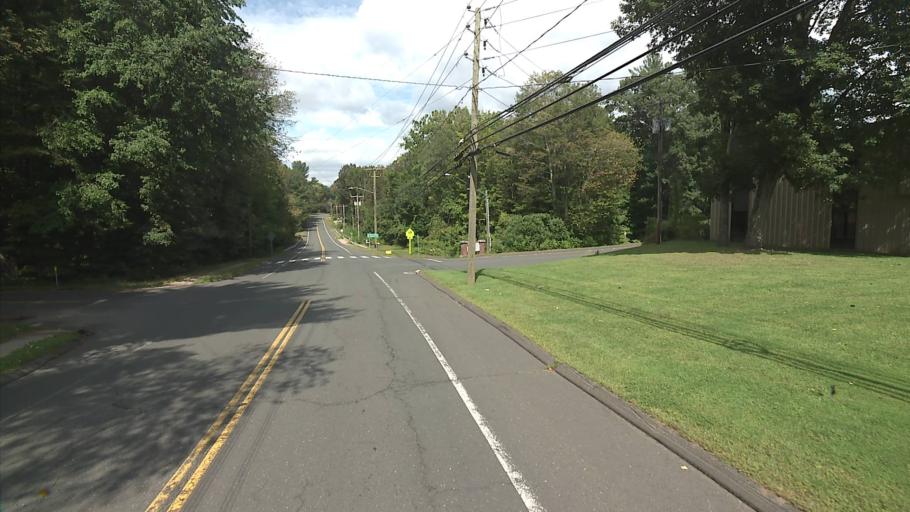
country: US
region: Connecticut
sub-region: Hartford County
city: Salmon Brook
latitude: 41.9590
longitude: -72.7957
